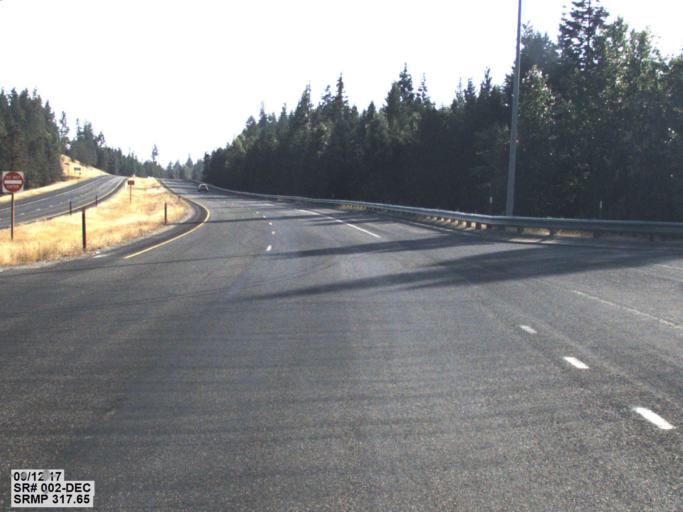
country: US
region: Washington
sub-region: Spokane County
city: Deer Park
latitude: 48.0751
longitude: -117.3316
